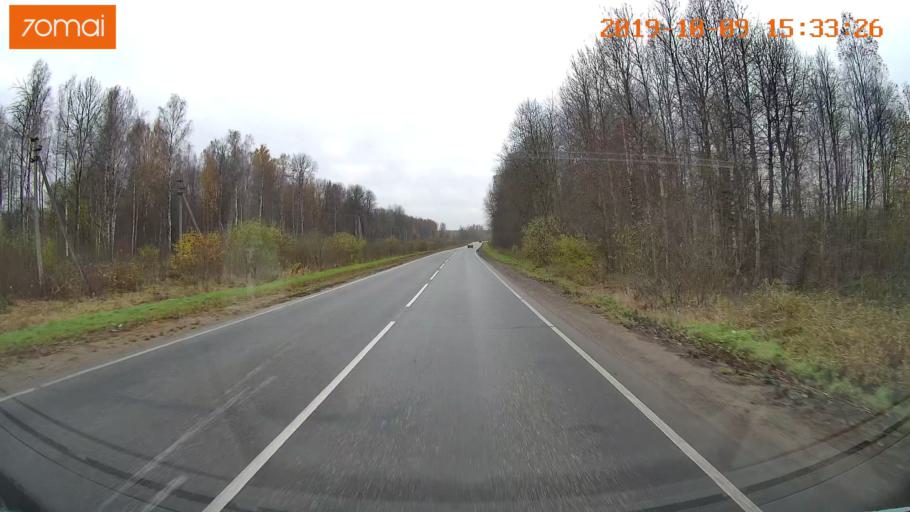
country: RU
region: Kostroma
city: Oktyabr'skiy
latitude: 57.9517
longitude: 41.2625
